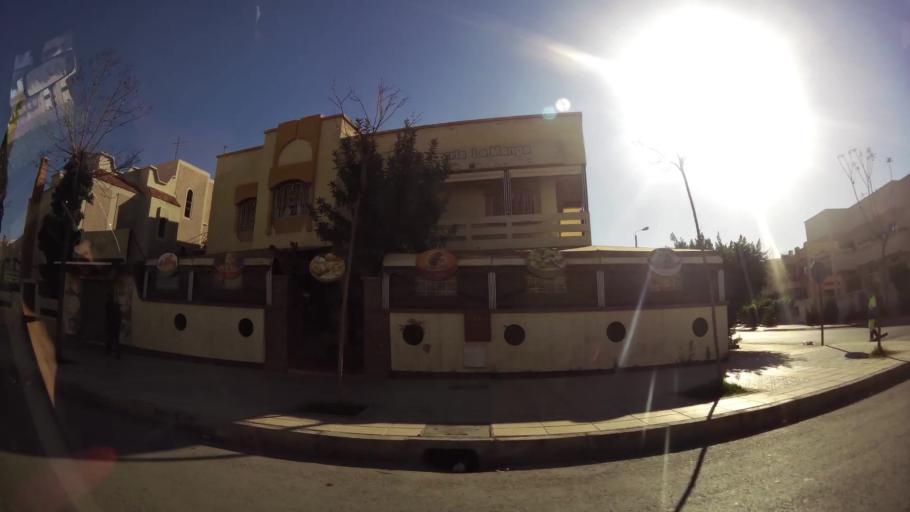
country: MA
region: Oriental
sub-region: Oujda-Angad
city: Oujda
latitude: 34.6578
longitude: -1.9015
